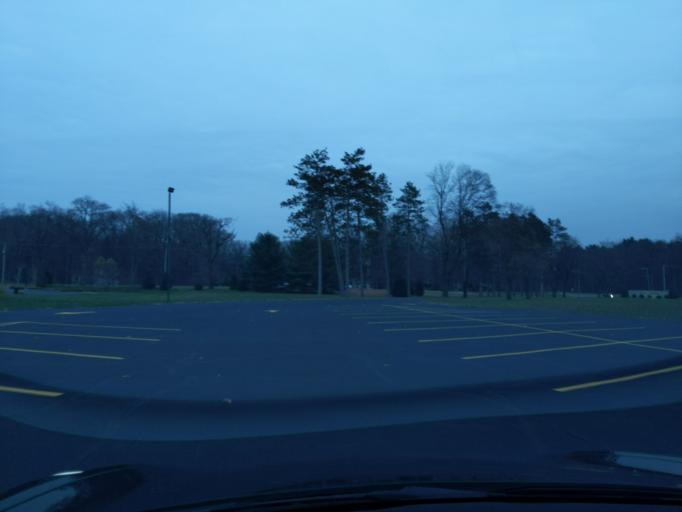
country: US
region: Indiana
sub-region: Saint Joseph County
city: Georgetown
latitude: 41.7317
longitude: -86.2675
